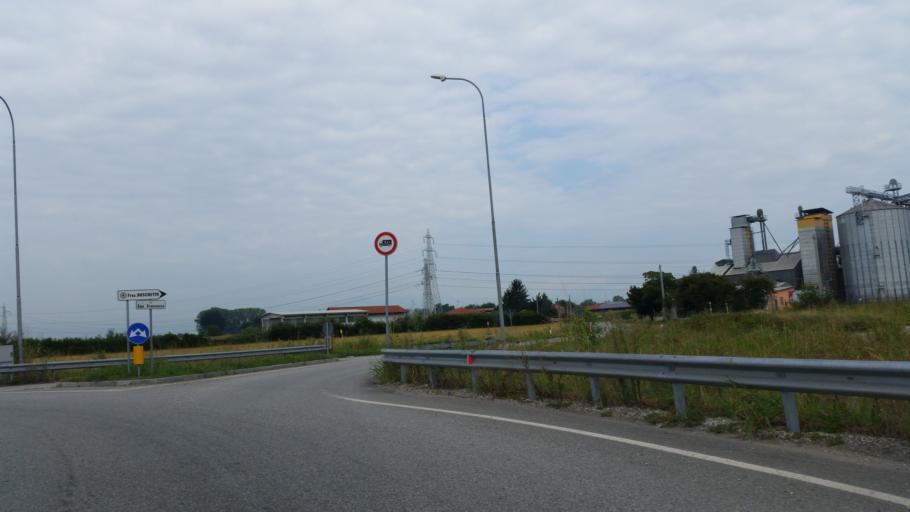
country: IT
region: Piedmont
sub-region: Provincia di Torino
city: Chivasso
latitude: 45.2289
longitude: 7.9109
